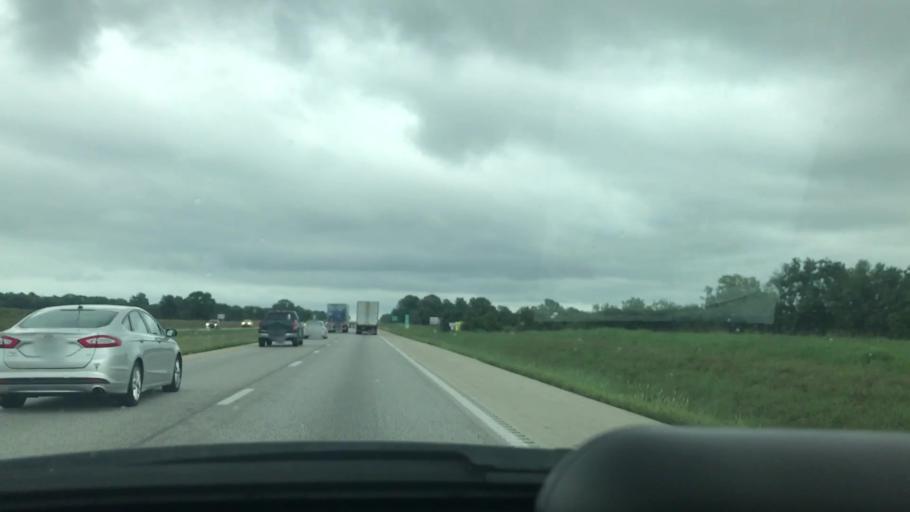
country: US
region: Missouri
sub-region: Greene County
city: Ash Grove
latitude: 37.1867
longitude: -93.6098
